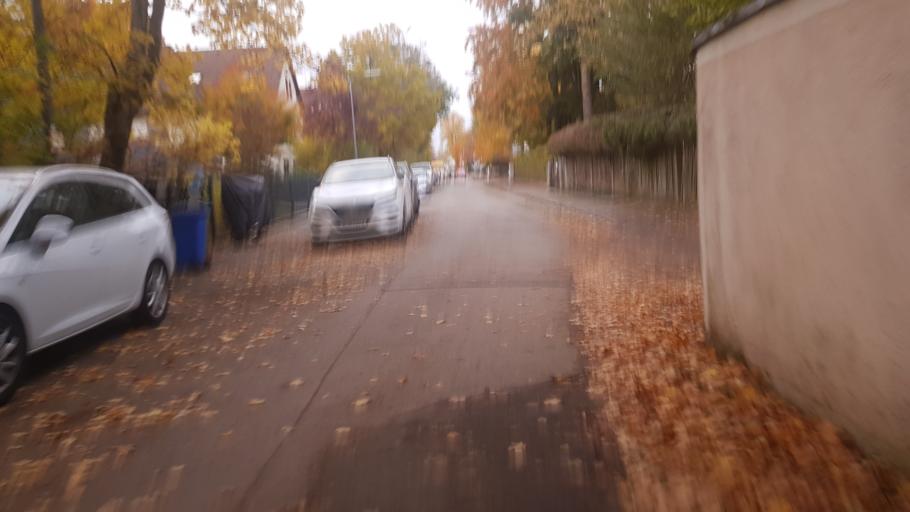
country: DE
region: Bavaria
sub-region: Upper Bavaria
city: Unterhaching
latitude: 48.0879
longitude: 11.6117
